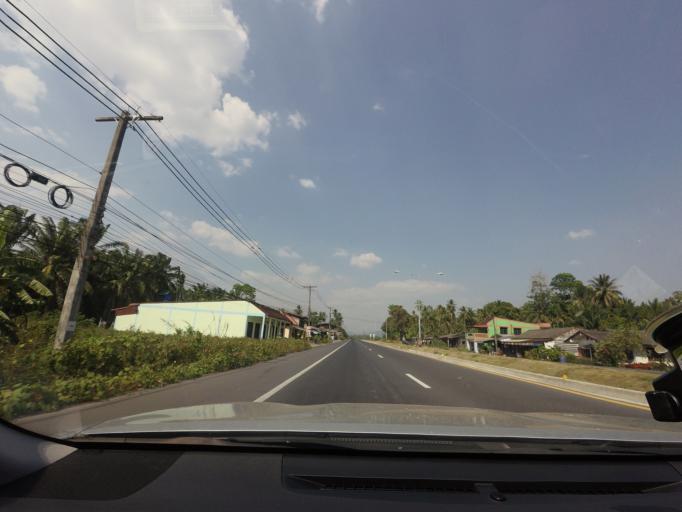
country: TH
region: Phangnga
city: Thap Put
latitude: 8.5444
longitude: 98.7264
